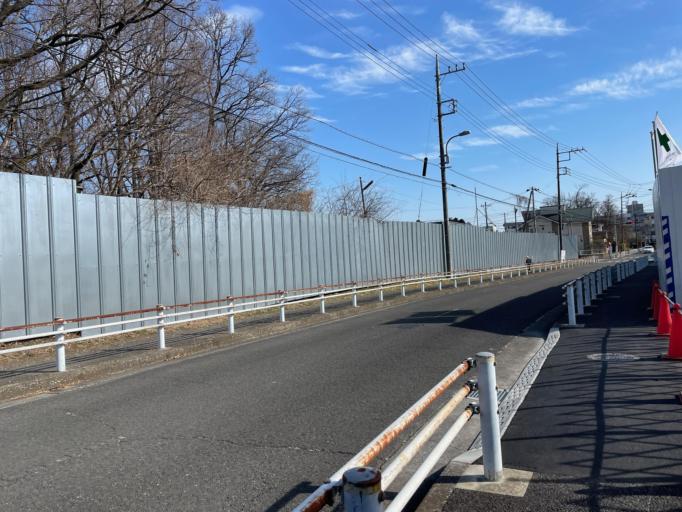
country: JP
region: Tokyo
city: Hachioji
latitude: 35.6780
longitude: 139.3060
